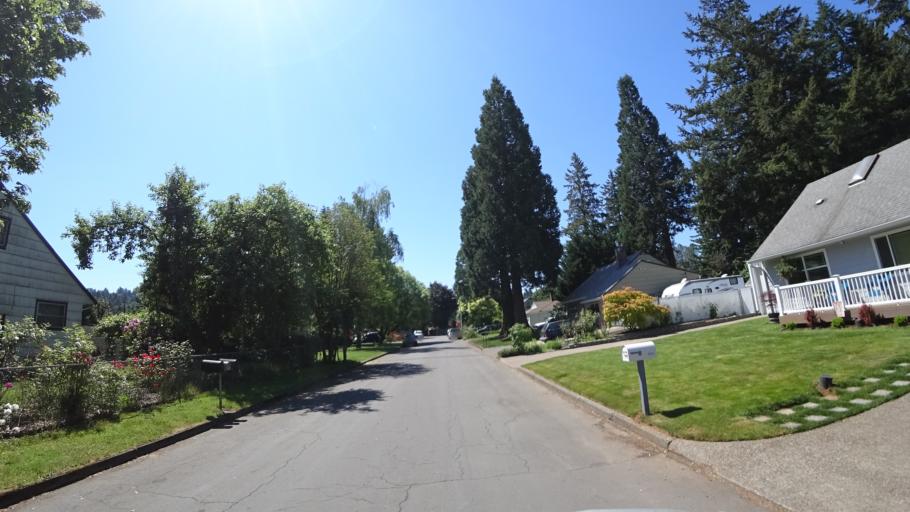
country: US
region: Oregon
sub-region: Clackamas County
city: Happy Valley
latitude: 45.4758
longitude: -122.5245
